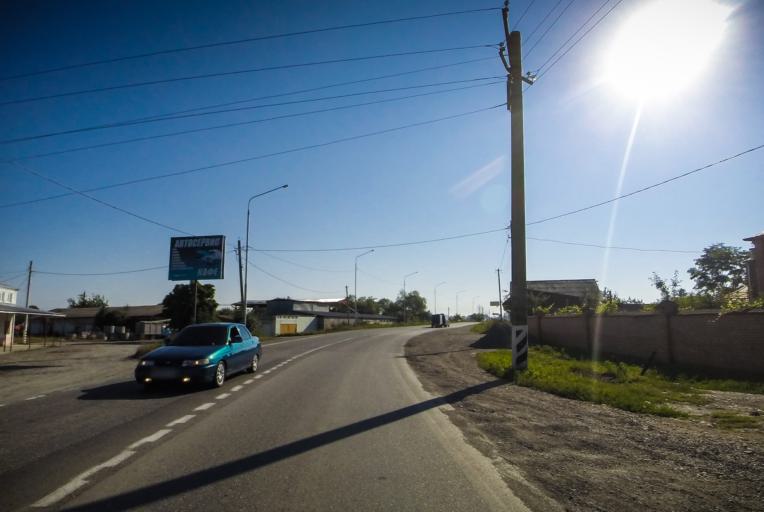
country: RU
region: North Ossetia
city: Arkhonskaya
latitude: 43.1169
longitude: 44.4979
